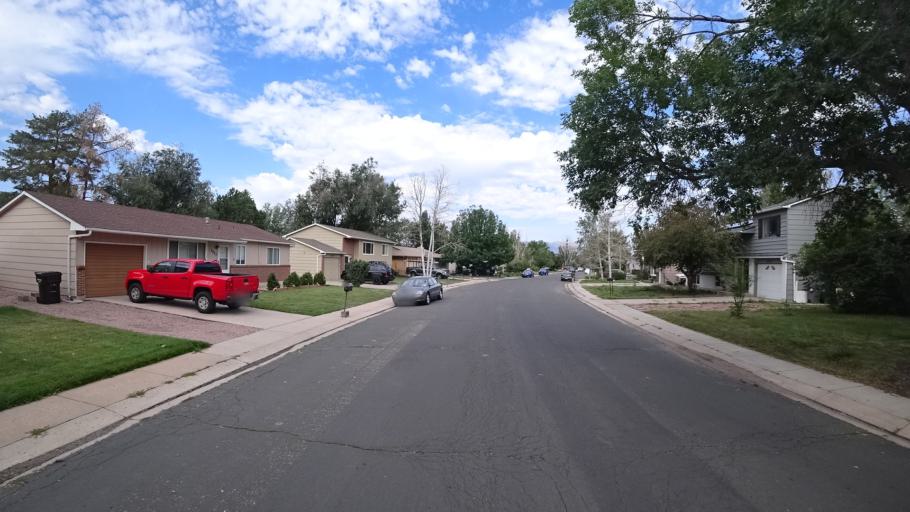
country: US
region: Colorado
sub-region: El Paso County
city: Cimarron Hills
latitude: 38.8978
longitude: -104.7536
